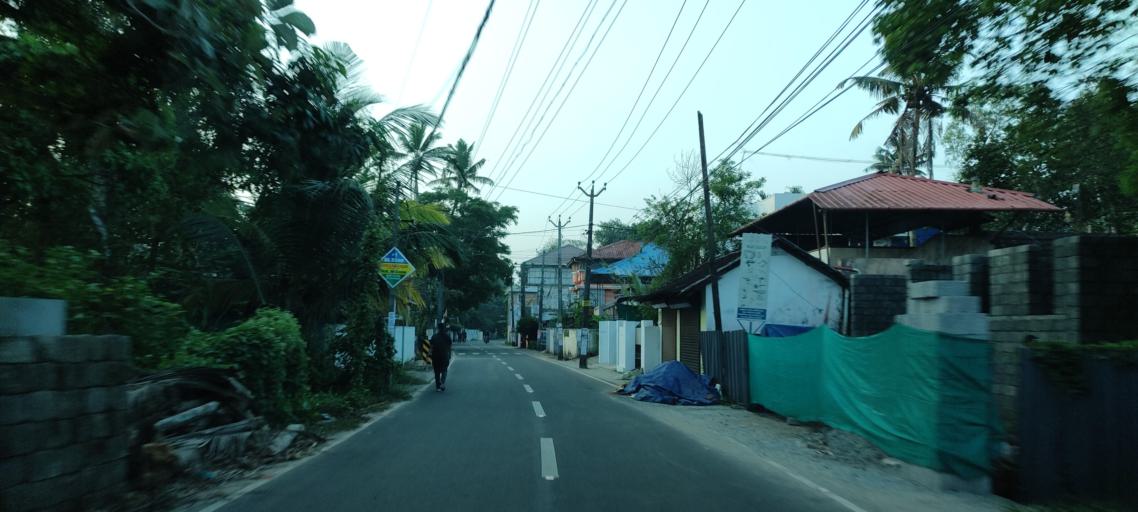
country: IN
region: Kerala
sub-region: Alappuzha
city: Alleppey
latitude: 9.4607
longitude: 76.3442
